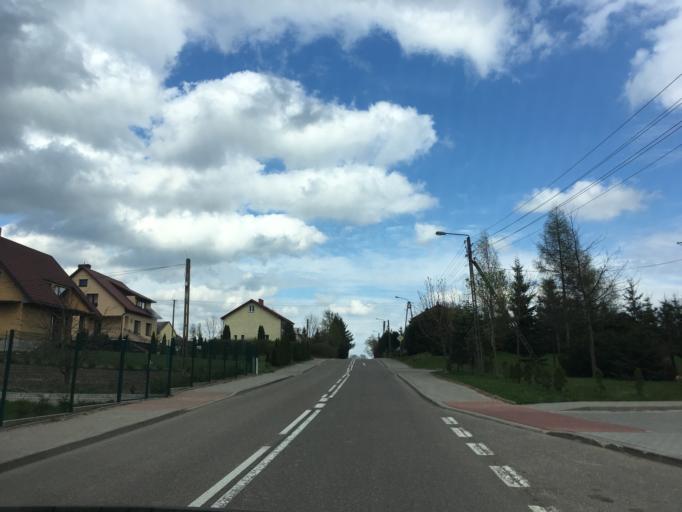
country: PL
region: Podlasie
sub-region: Suwalki
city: Suwalki
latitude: 54.3637
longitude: 22.8610
